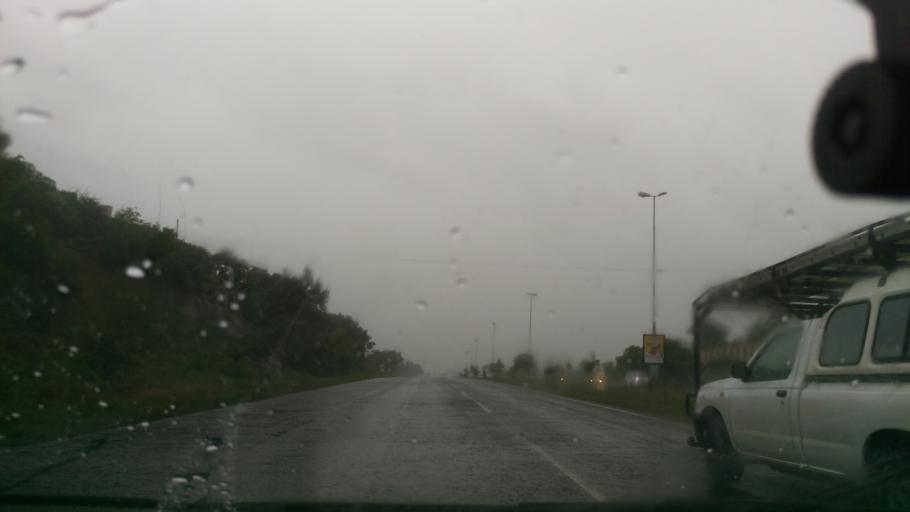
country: ZA
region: Gauteng
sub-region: West Rand District Municipality
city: Muldersdriseloop
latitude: -26.0663
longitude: 27.9402
